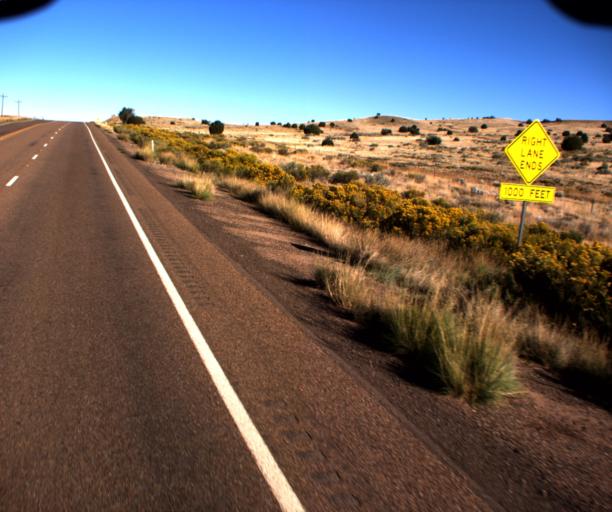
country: US
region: Arizona
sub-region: Navajo County
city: Taylor
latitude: 34.4275
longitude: -110.0904
